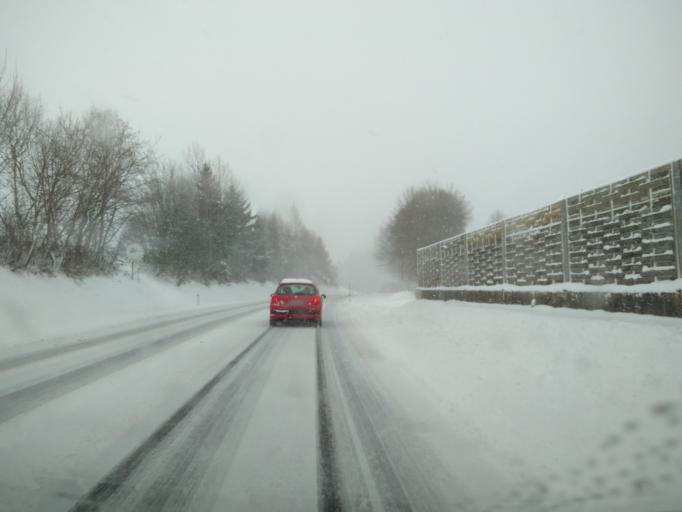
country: AT
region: Upper Austria
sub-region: Politischer Bezirk Urfahr-Umgebung
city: Bad Leonfelden
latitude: 48.4993
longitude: 14.3002
